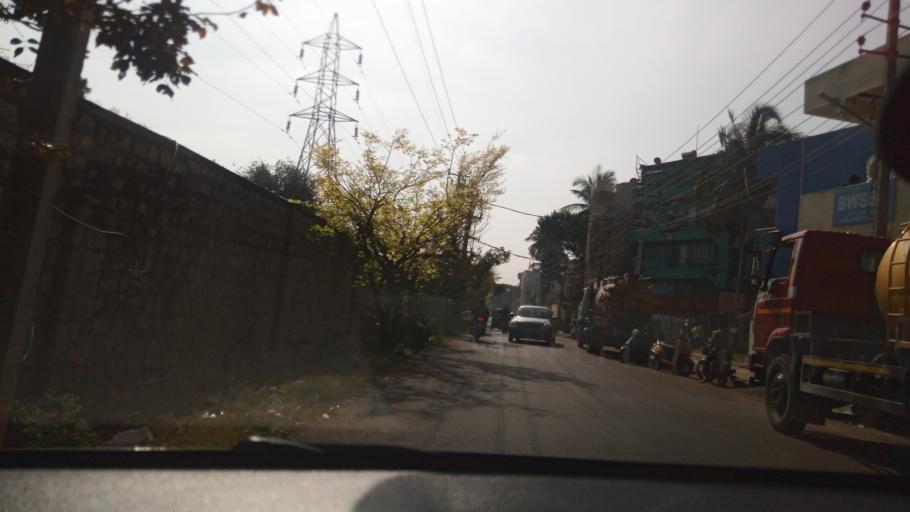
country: IN
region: Karnataka
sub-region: Bangalore Urban
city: Yelahanka
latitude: 13.0457
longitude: 77.5521
